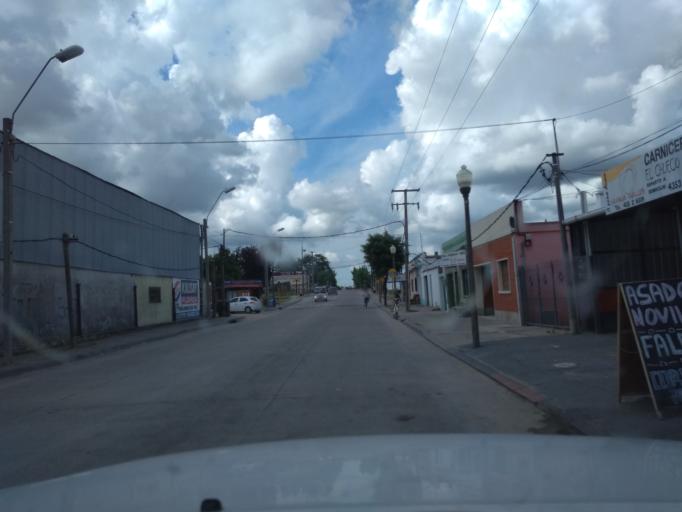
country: UY
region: Florida
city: Florida
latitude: -34.0884
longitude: -56.2144
